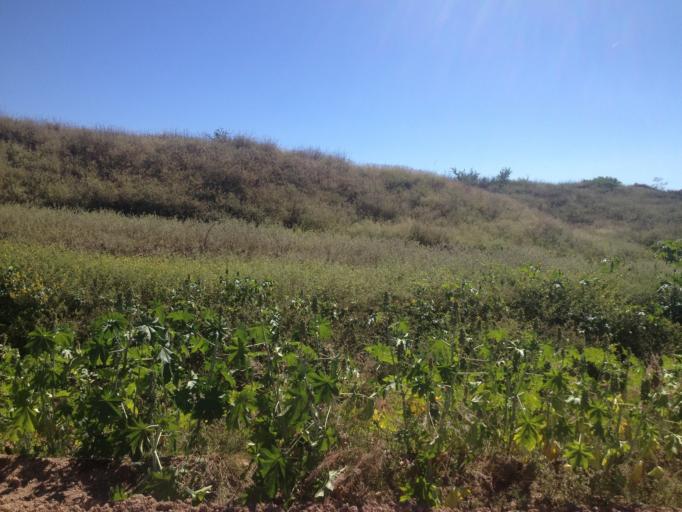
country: MX
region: Aguascalientes
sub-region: Aguascalientes
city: San Sebastian [Fraccionamiento]
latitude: 21.8358
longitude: -102.2494
